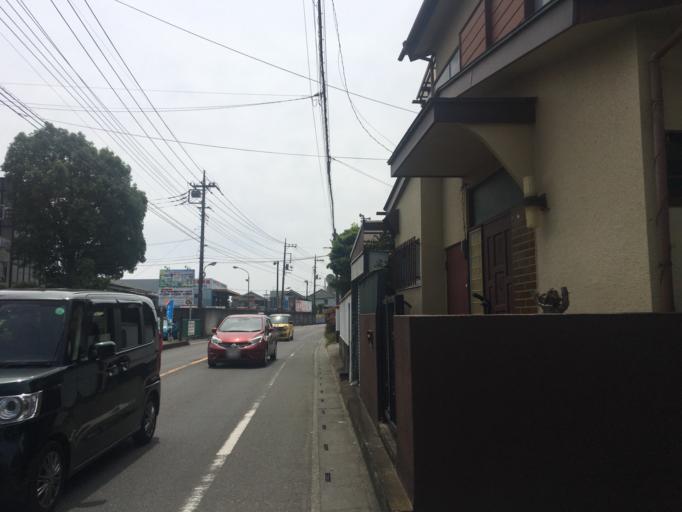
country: JP
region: Saitama
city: Sayama
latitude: 35.8459
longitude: 139.4254
